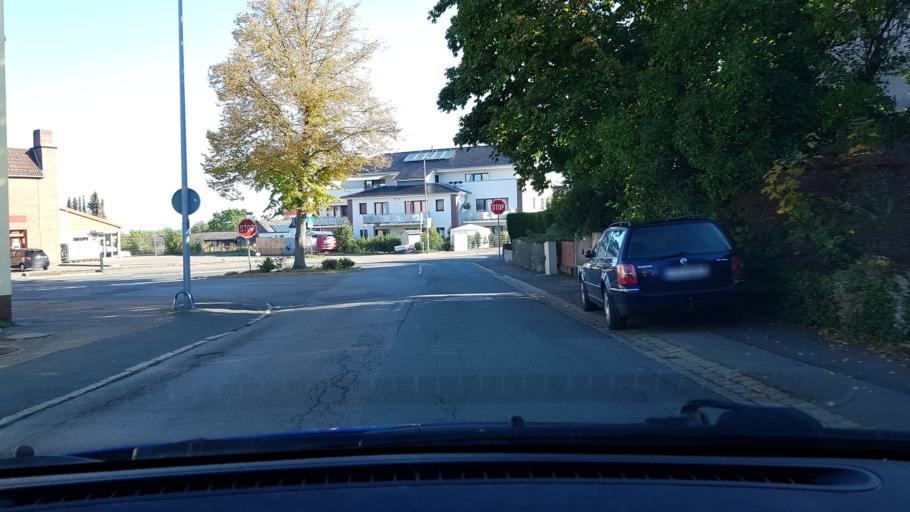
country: DE
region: Lower Saxony
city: Egestorf
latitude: 52.2889
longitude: 9.5021
